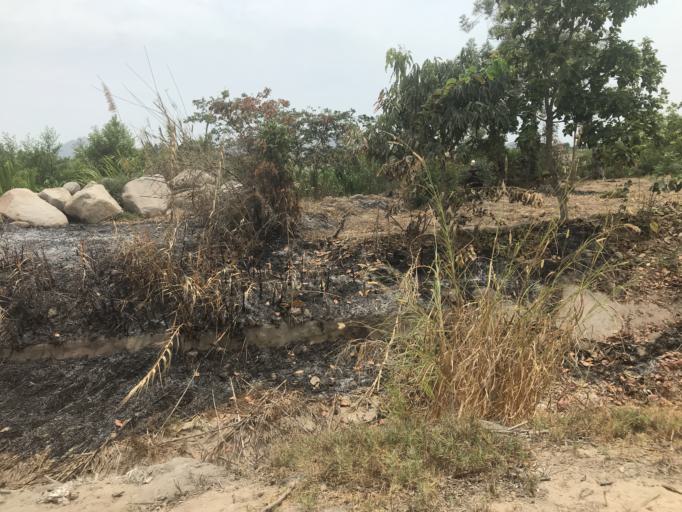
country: PE
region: La Libertad
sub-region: Viru
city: Viru
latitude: -8.4223
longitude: -78.7944
